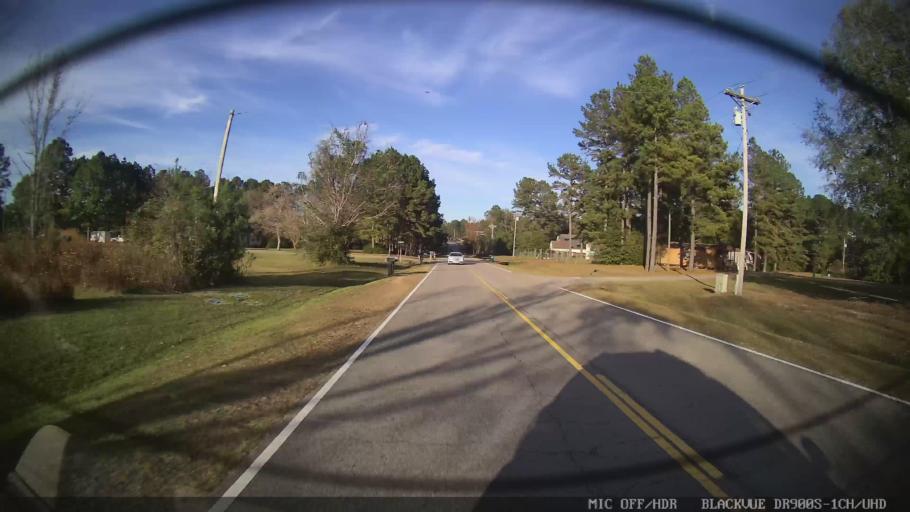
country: US
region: Mississippi
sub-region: Lamar County
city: Purvis
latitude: 31.1871
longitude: -89.2896
